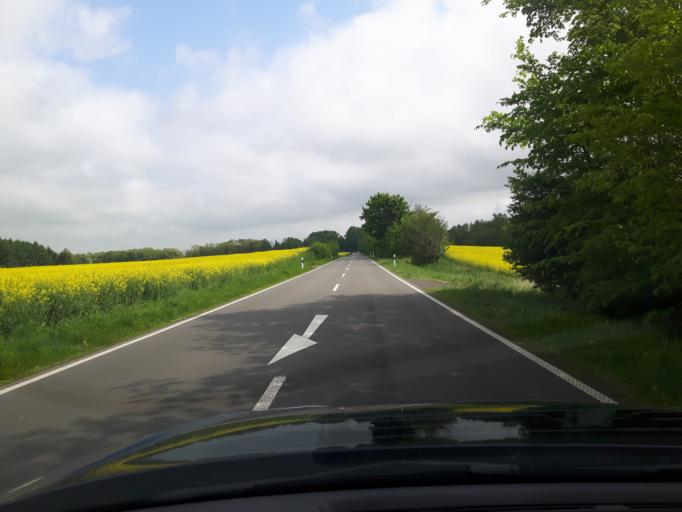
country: DE
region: Mecklenburg-Vorpommern
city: Gross Wokern
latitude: 53.6363
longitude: 12.4796
